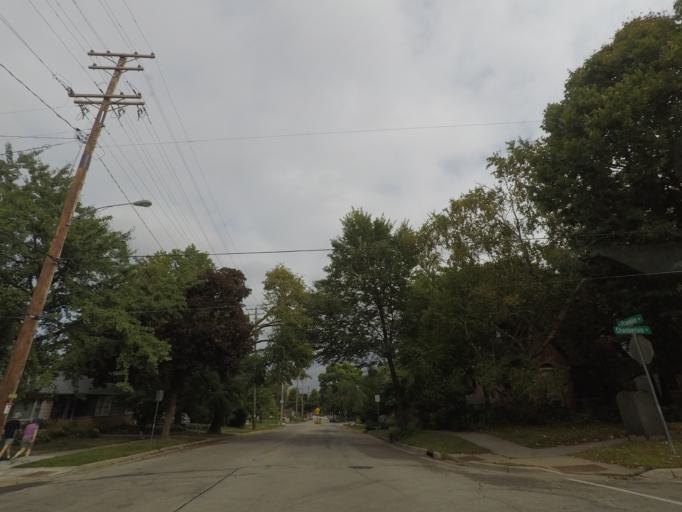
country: US
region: Wisconsin
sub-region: Dane County
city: Shorewood Hills
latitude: 43.0696
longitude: -89.4363
